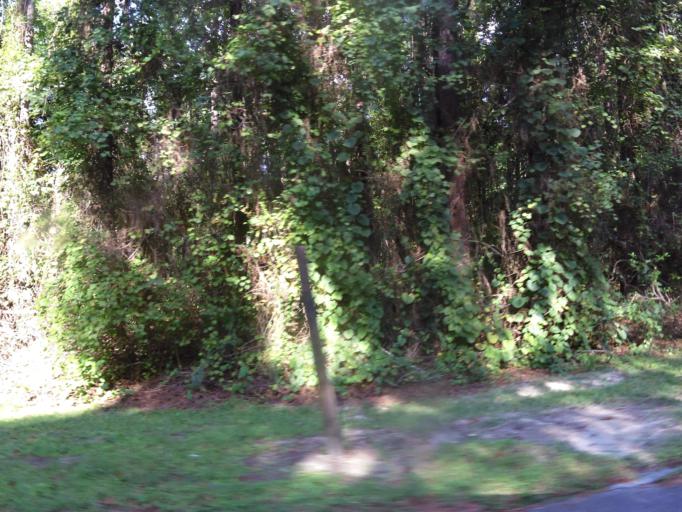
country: US
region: Florida
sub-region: Clay County
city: Orange Park
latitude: 30.2384
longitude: -81.6994
